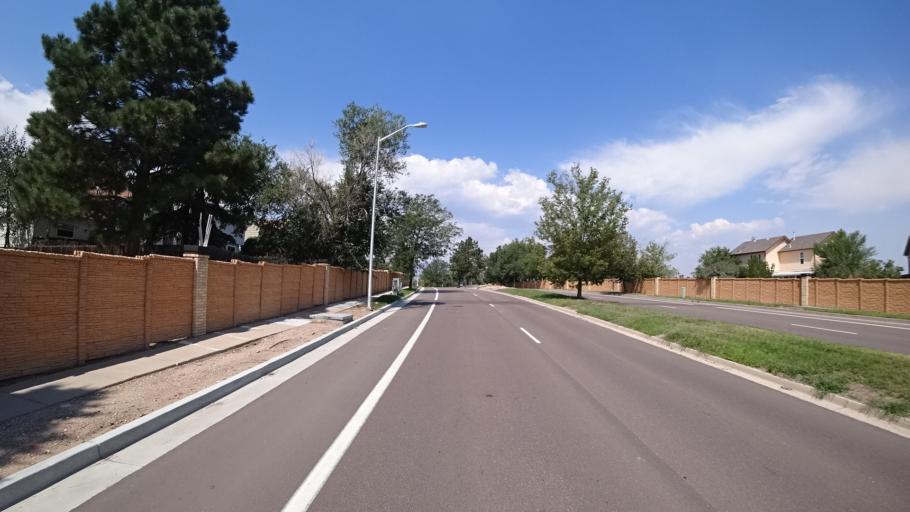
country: US
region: Colorado
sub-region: El Paso County
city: Cimarron Hills
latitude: 38.9250
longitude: -104.7625
